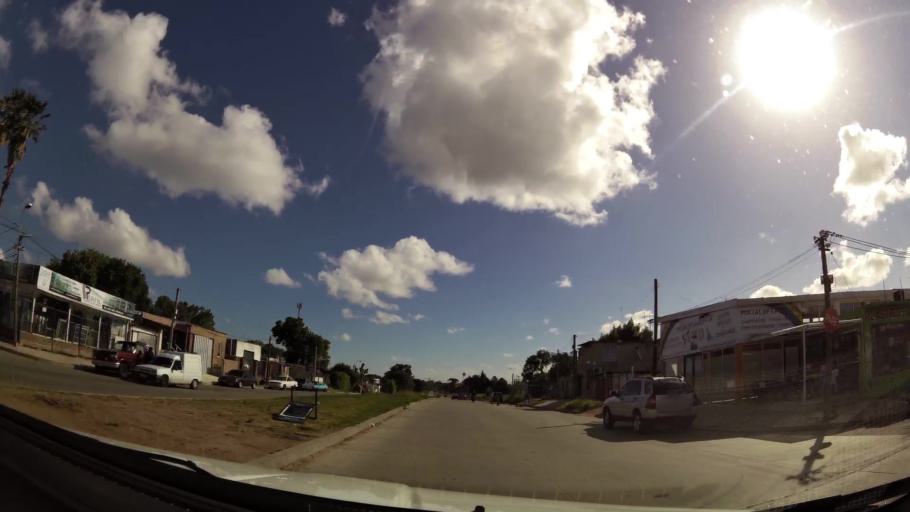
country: UY
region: Canelones
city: La Paz
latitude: -34.8140
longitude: -56.2311
